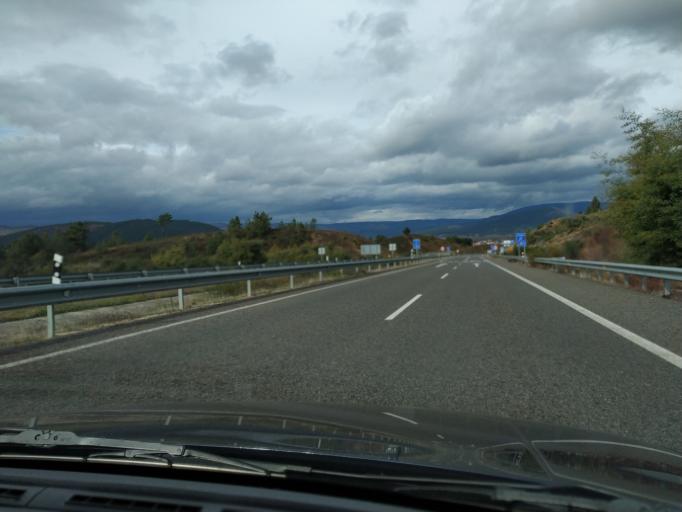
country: ES
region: Galicia
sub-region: Provincia de Ourense
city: Verin
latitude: 41.9040
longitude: -7.4283
